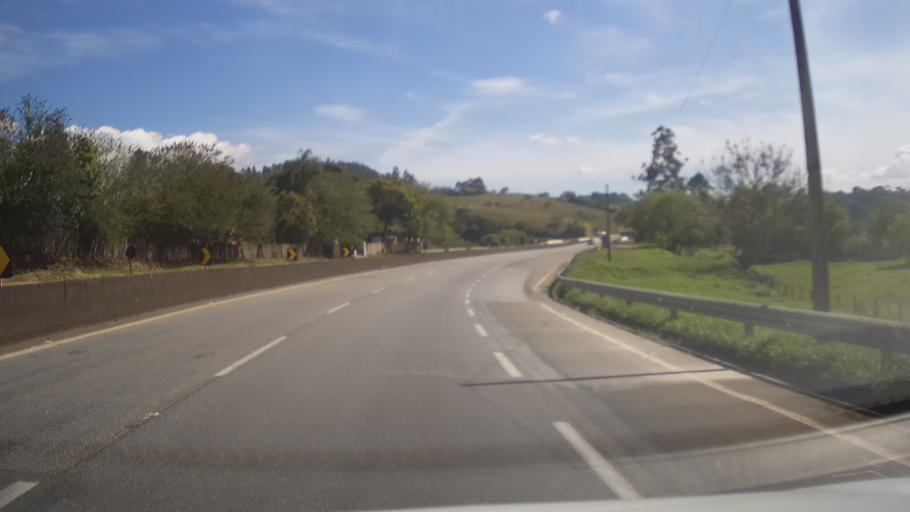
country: BR
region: Minas Gerais
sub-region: Cambui
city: Cambui
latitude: -22.5394
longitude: -46.0372
